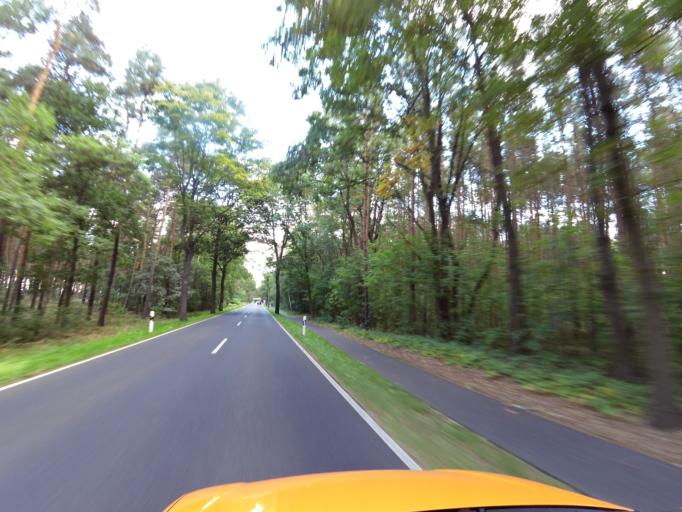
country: DE
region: Brandenburg
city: Luckenwalde
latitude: 52.1140
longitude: 13.1699
